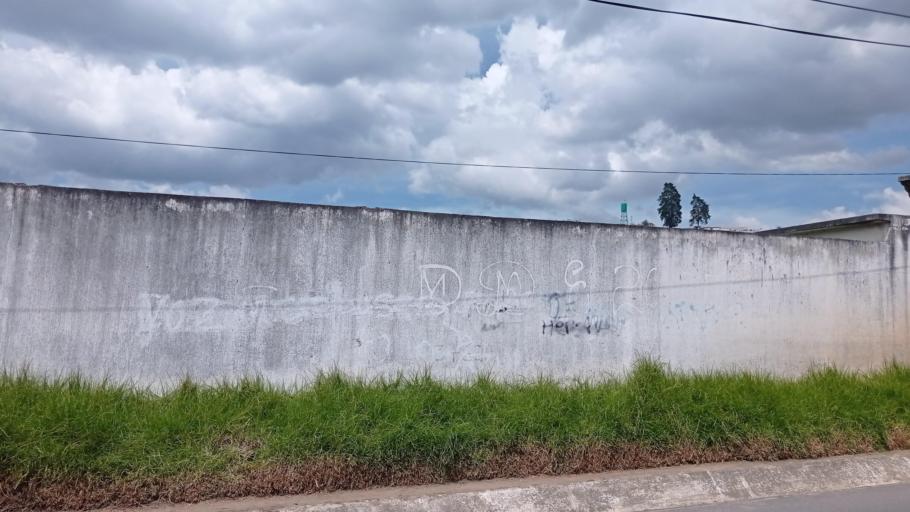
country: GT
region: Quetzaltenango
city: Quetzaltenango
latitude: 14.8502
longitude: -91.5004
